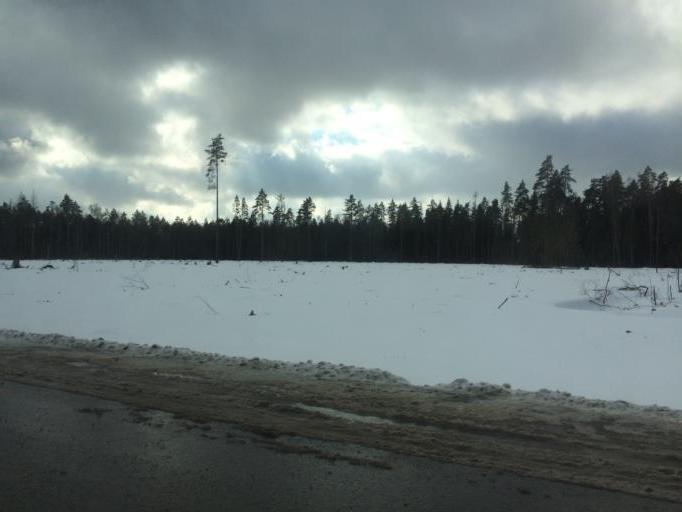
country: RU
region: Moskovskaya
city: Petrovo-Dal'neye
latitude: 55.7934
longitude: 37.1493
